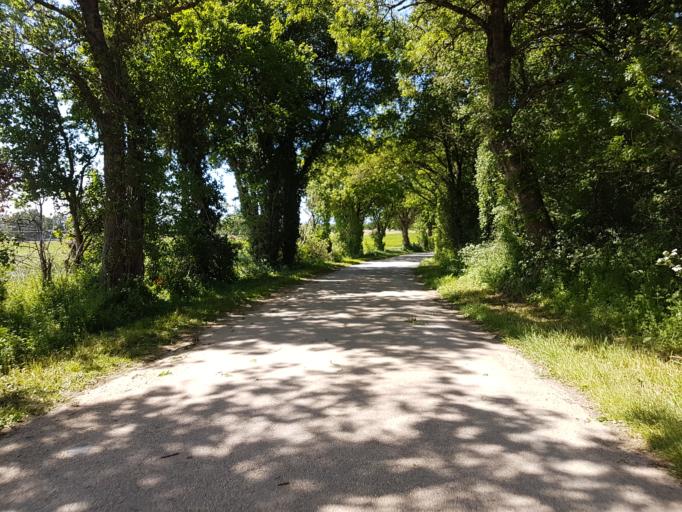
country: FR
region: Rhone-Alpes
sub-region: Departement du Rhone
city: Jons
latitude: 45.7848
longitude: 5.0882
